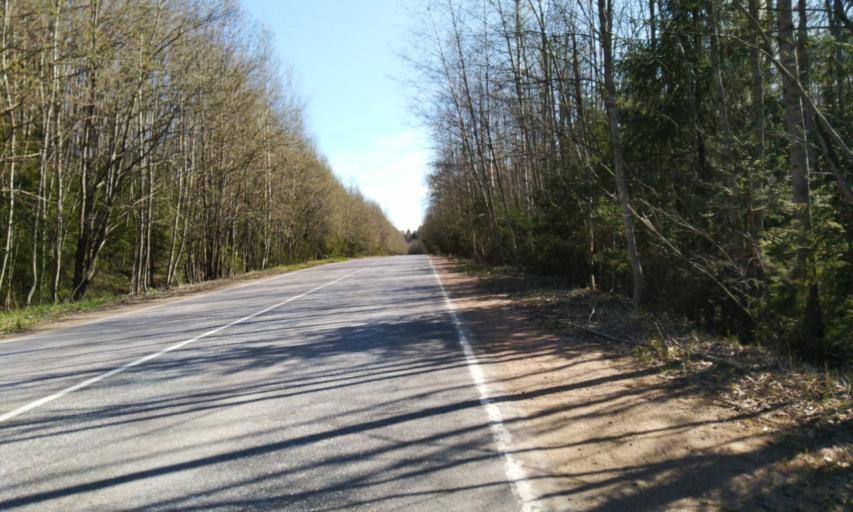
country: RU
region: Leningrad
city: Garbolovo
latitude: 60.3737
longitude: 30.4485
